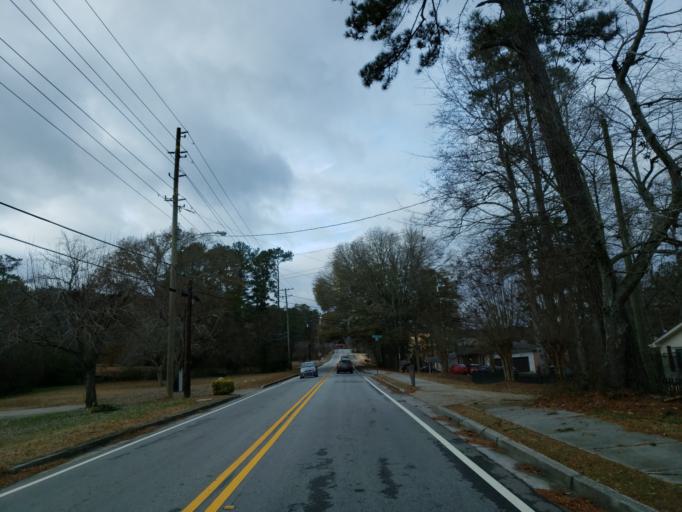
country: US
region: Georgia
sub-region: Cobb County
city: Fair Oaks
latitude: 33.8896
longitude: -84.6066
